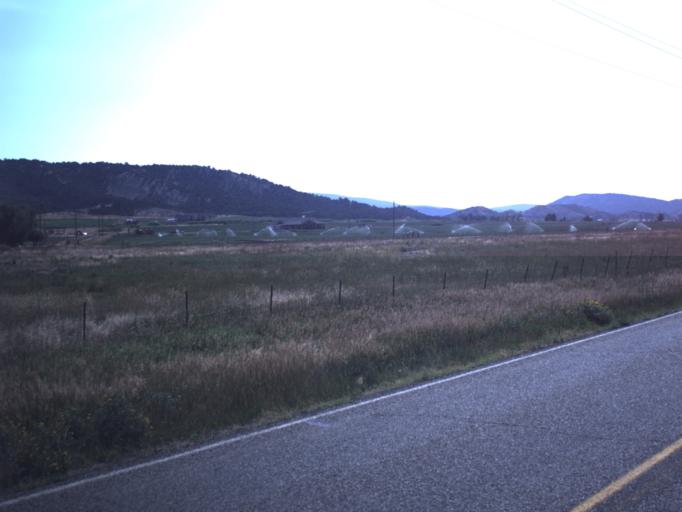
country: US
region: Utah
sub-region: Duchesne County
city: Duchesne
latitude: 40.3857
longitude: -110.7436
